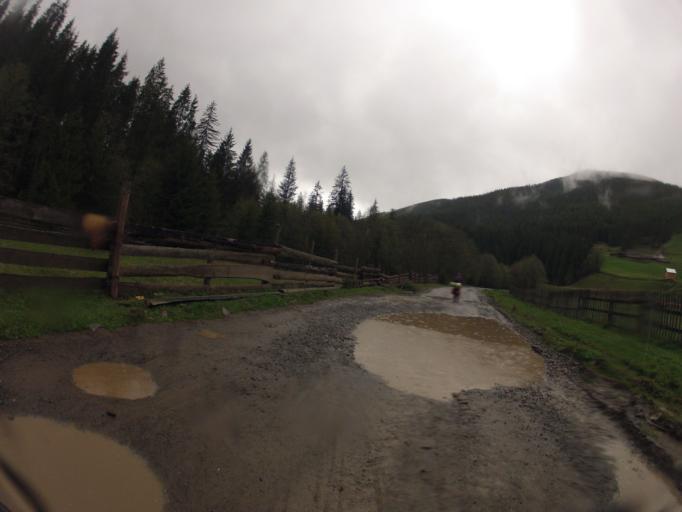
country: RO
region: Suceava
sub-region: Comuna Izvoarele Sucevei
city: Izvoarele Sucevei
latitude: 47.8326
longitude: 25.0492
